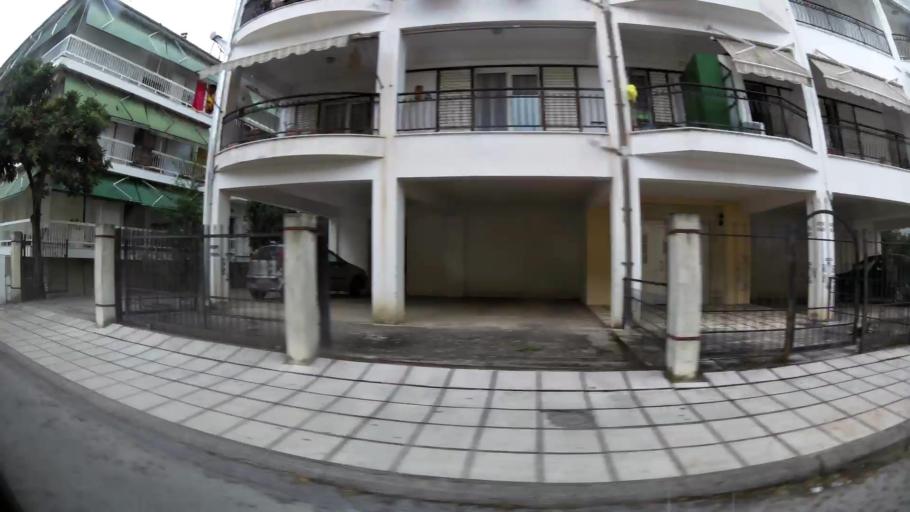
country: GR
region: Central Macedonia
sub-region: Nomos Imathias
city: Veroia
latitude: 40.5287
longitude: 22.1969
